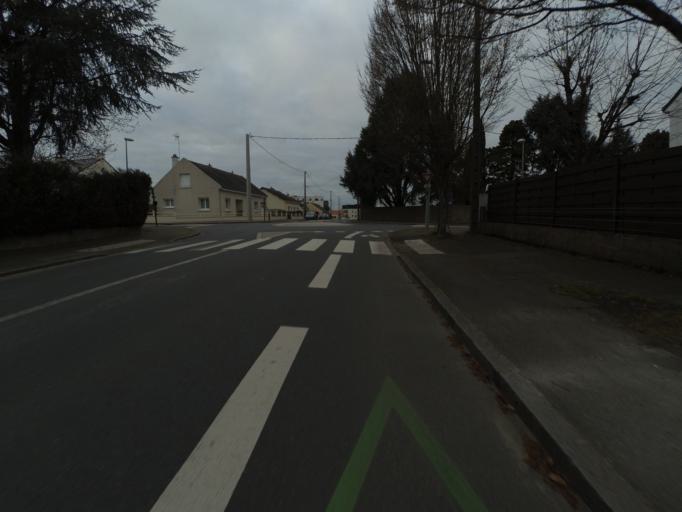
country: FR
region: Pays de la Loire
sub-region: Departement de la Loire-Atlantique
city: Carquefou
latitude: 47.2986
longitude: -1.4882
